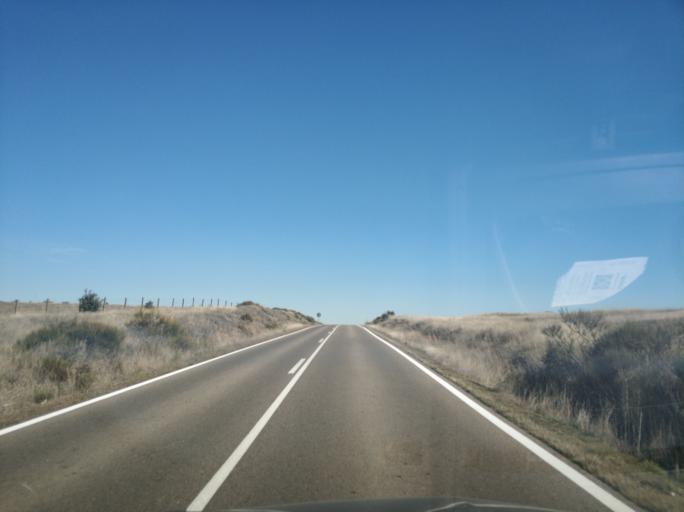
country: ES
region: Castille and Leon
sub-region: Provincia de Salamanca
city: Aldeatejada
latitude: 40.9397
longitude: -5.7139
